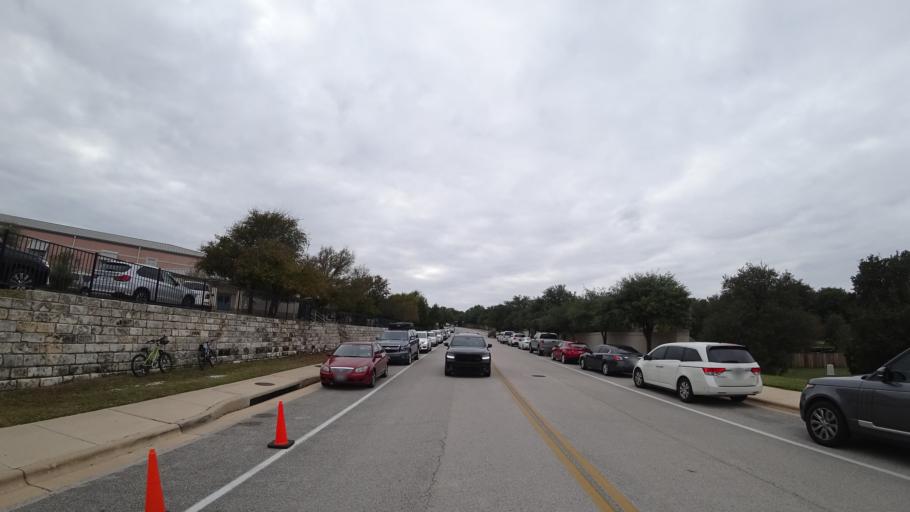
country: US
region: Texas
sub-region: Travis County
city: Bee Cave
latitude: 30.3101
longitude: -97.9205
